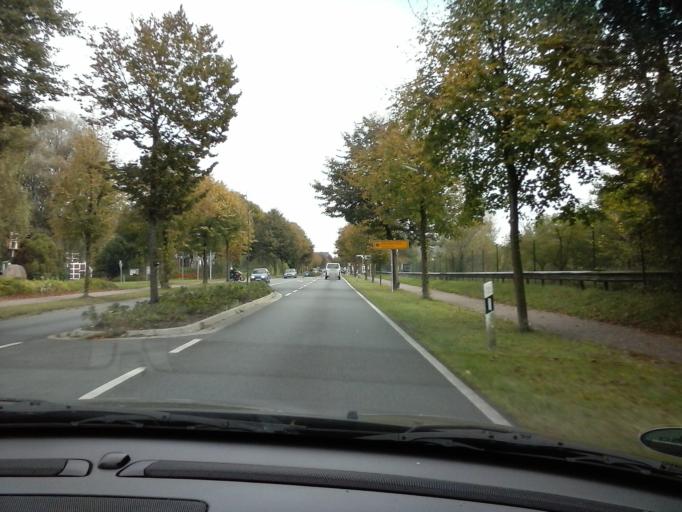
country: DE
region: Lower Saxony
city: Hemmoor
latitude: 53.7030
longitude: 9.1307
